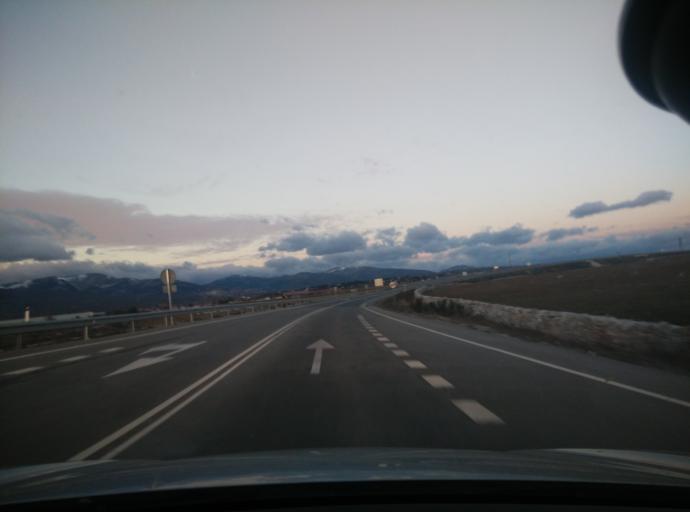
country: ES
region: Madrid
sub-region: Provincia de Madrid
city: Colmenar Viejo
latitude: 40.7233
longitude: -3.7910
